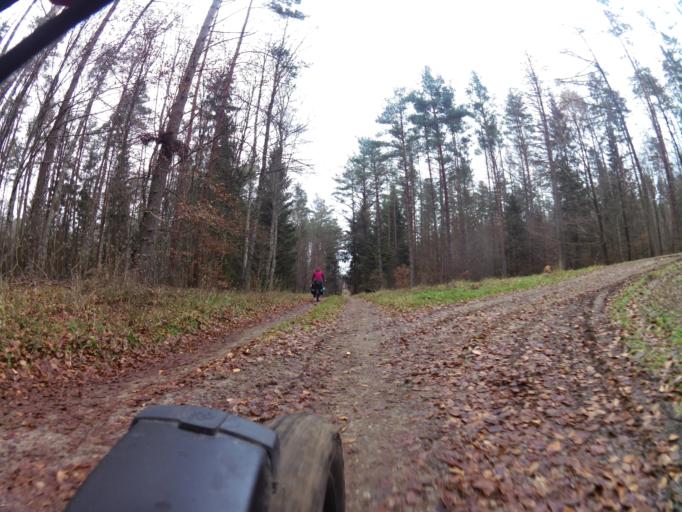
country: PL
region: West Pomeranian Voivodeship
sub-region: Powiat koszalinski
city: Polanow
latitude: 54.0464
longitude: 16.6595
